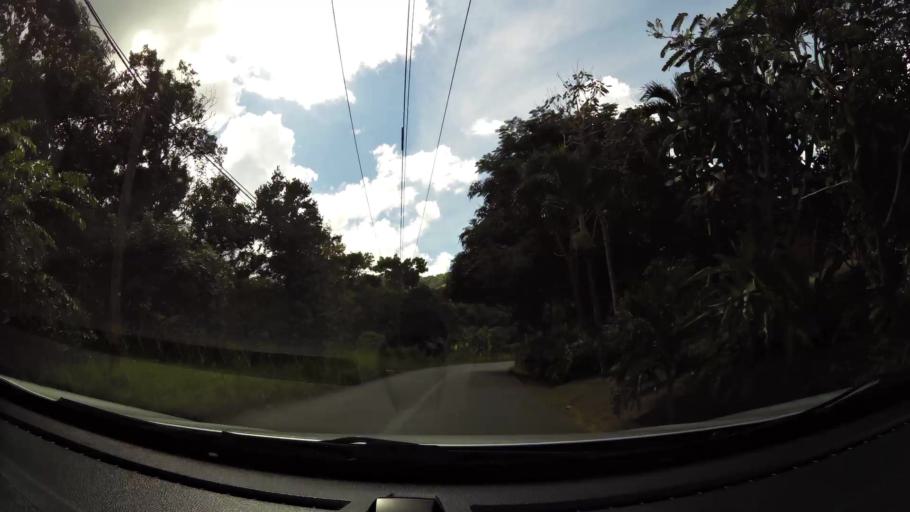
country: CR
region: San Jose
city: San Isidro
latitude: 9.3482
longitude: -83.7355
